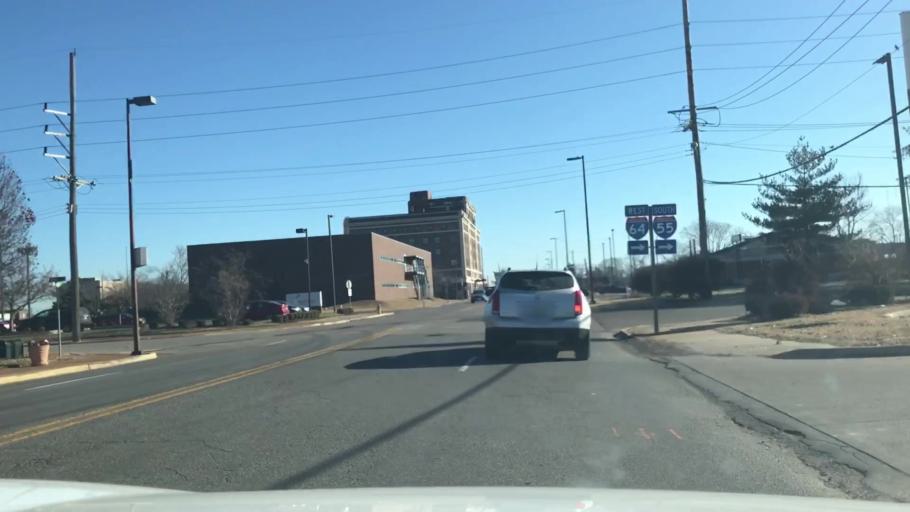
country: US
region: Illinois
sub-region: Saint Clair County
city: East Saint Louis
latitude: 38.6261
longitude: -90.1631
